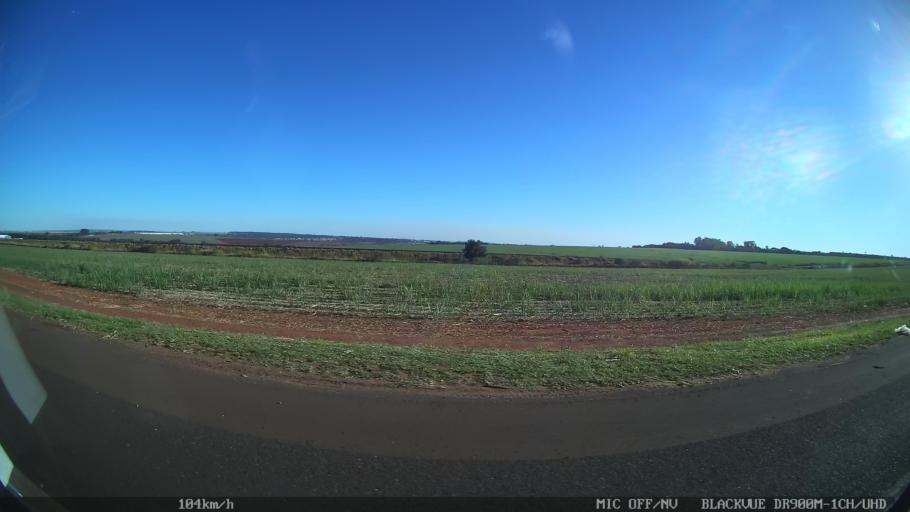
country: BR
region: Sao Paulo
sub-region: Americo Brasiliense
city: Americo Brasiliense
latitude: -21.7683
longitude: -48.1082
